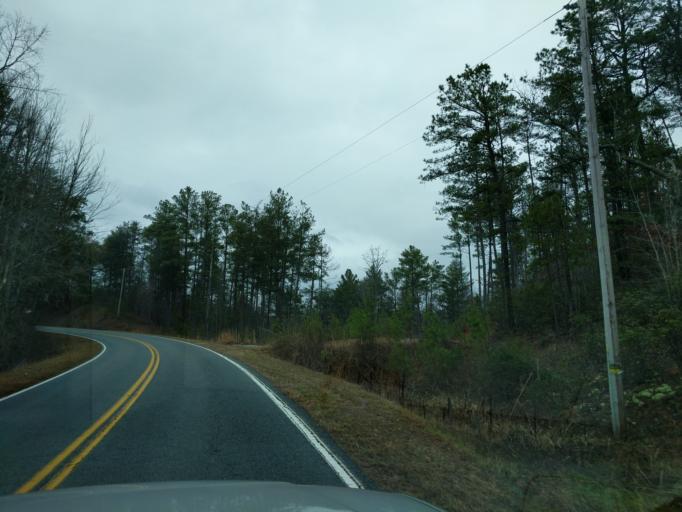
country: US
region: South Carolina
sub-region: Oconee County
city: Walhalla
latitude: 34.7924
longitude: -83.2184
